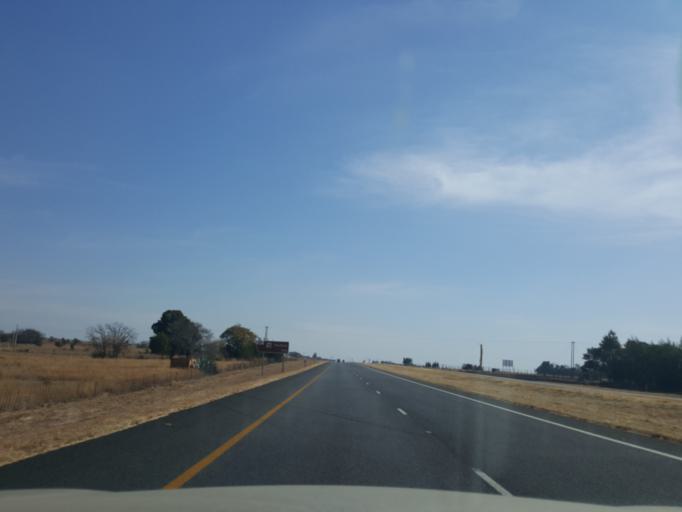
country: ZA
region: Gauteng
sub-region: City of Tshwane Metropolitan Municipality
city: Cullinan
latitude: -25.7987
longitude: 28.5832
